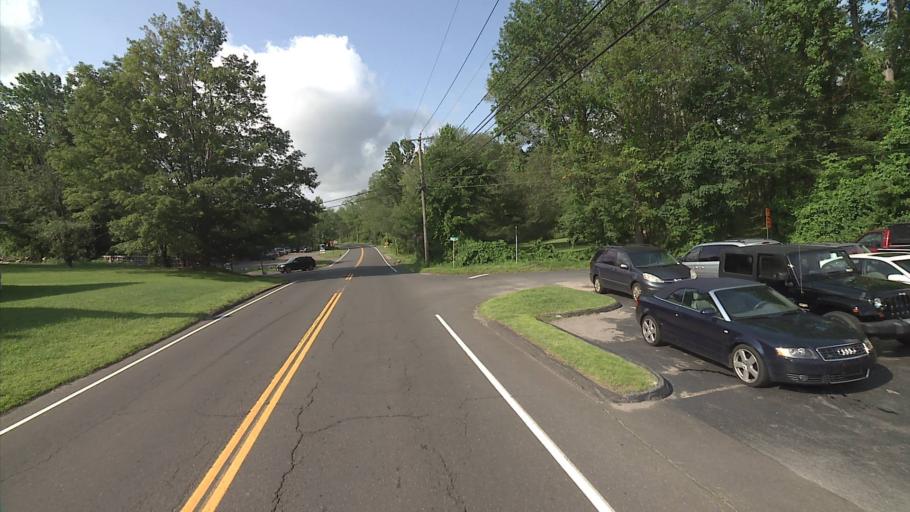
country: US
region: Connecticut
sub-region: Middlesex County
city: Higganum
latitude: 41.4320
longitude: -72.5594
